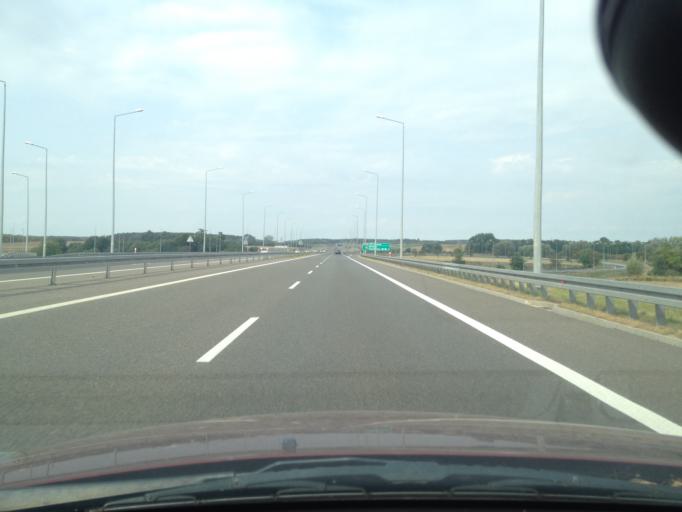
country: PL
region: West Pomeranian Voivodeship
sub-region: Powiat pyrzycki
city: Lipiany
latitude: 52.9504
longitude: 14.9545
